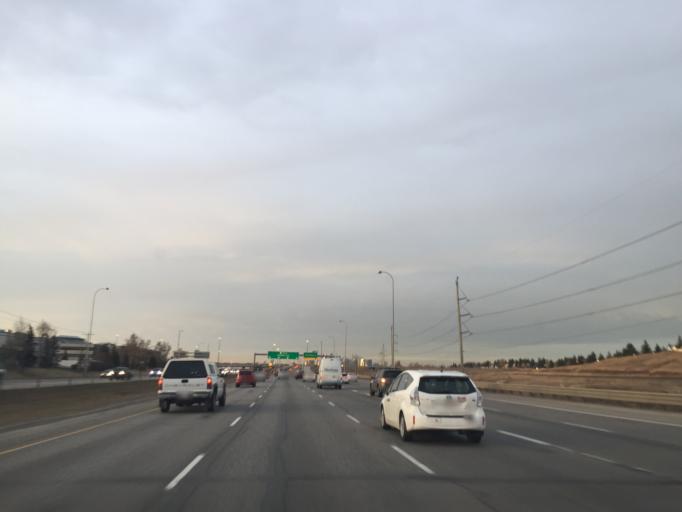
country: CA
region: Alberta
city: Calgary
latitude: 51.1177
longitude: -114.0468
